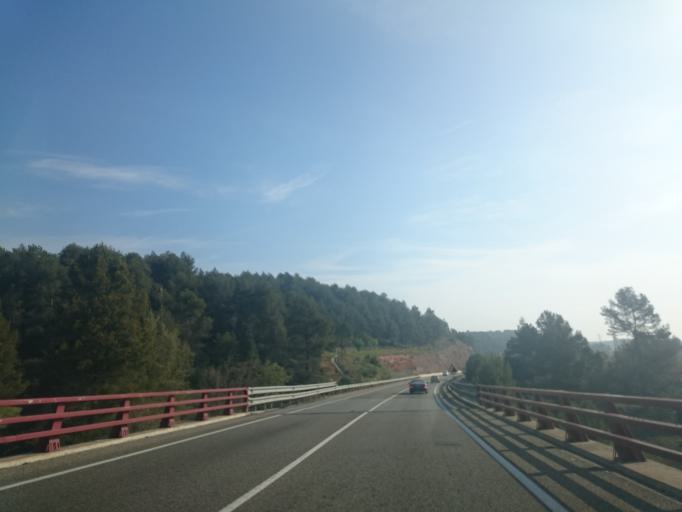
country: ES
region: Catalonia
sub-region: Provincia de Barcelona
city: Sant Salvador de Guardiola
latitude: 41.6866
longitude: 1.7570
